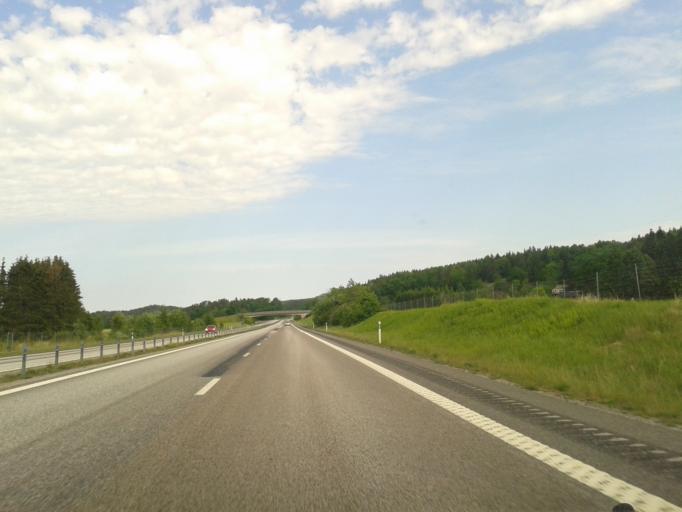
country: SE
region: Vaestra Goetaland
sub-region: Munkedals Kommun
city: Munkedal
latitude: 58.5325
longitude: 11.5364
